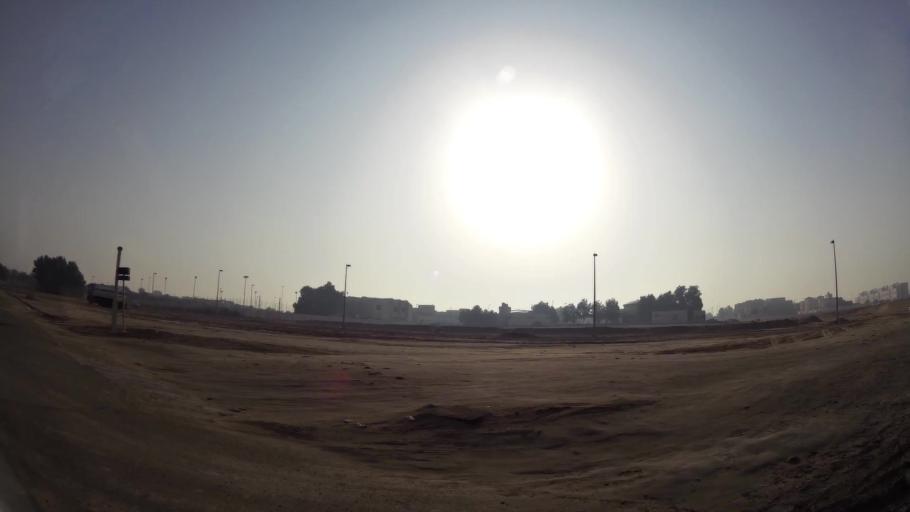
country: AE
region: Abu Dhabi
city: Abu Dhabi
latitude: 24.2829
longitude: 54.6406
